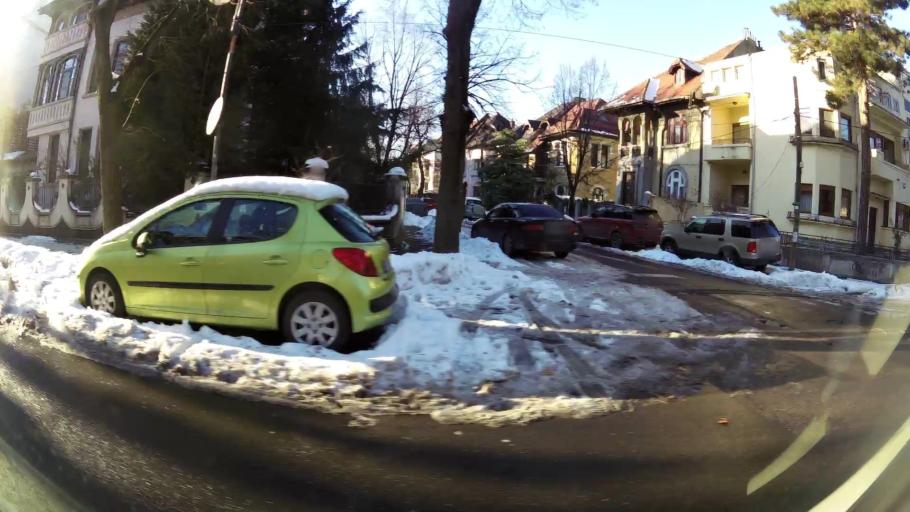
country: RO
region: Bucuresti
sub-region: Municipiul Bucuresti
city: Bucuresti
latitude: 44.4285
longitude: 26.0736
